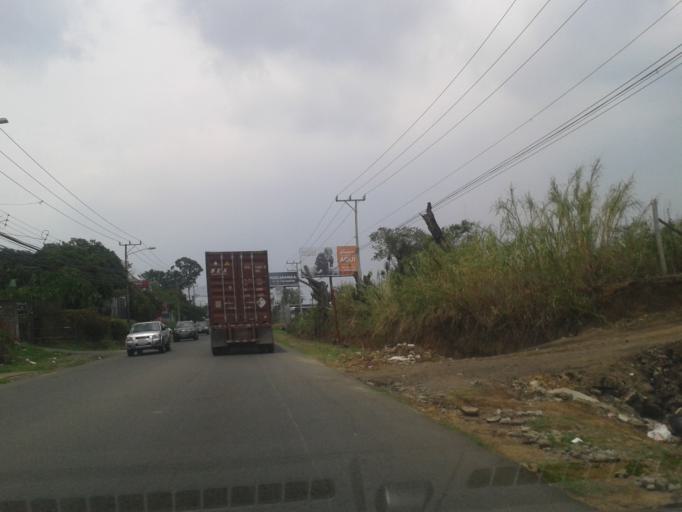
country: CR
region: Heredia
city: San Francisco
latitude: 9.9690
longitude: -84.1301
